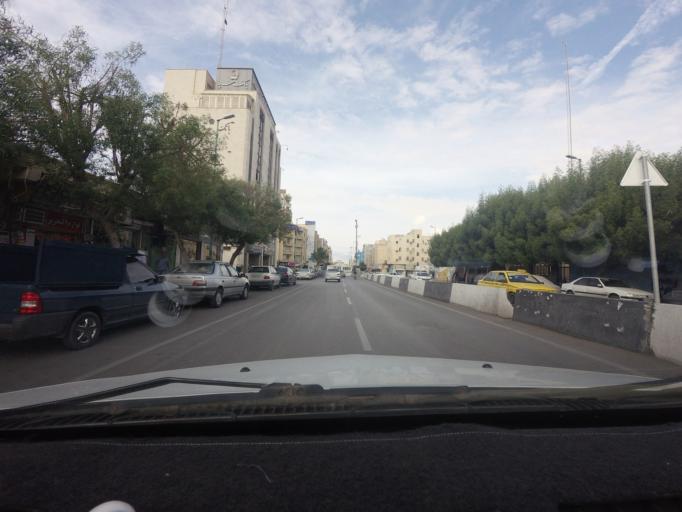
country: IR
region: Hormozgan
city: Bandar 'Abbas
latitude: 27.1830
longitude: 56.2776
